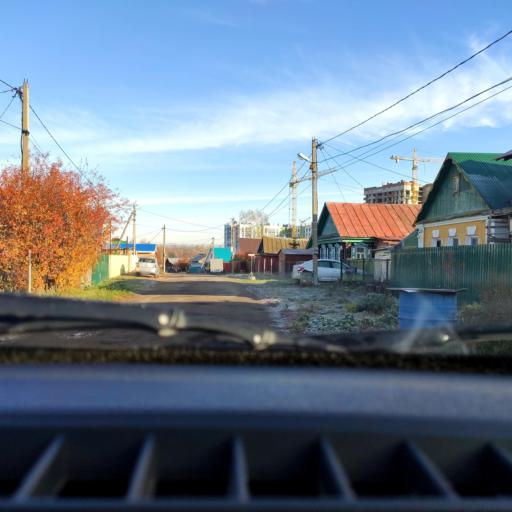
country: RU
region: Bashkortostan
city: Avdon
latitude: 54.7073
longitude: 55.8080
